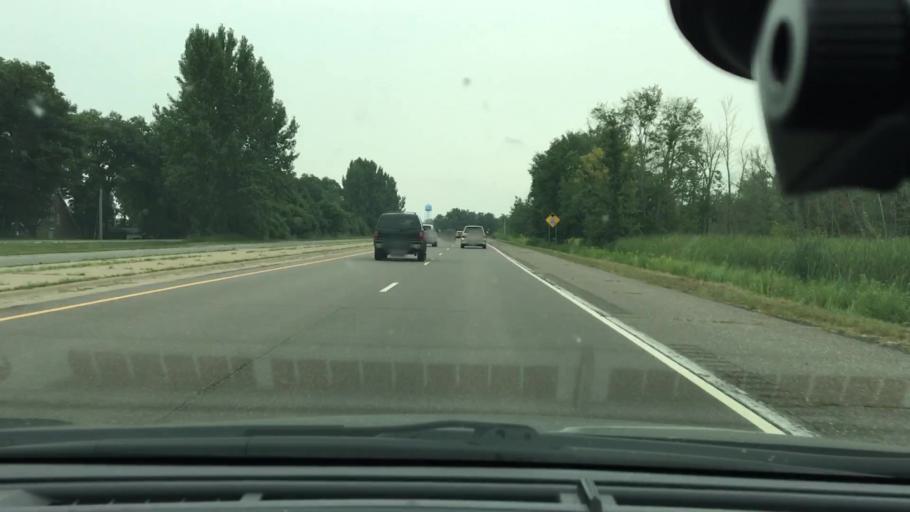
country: US
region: Minnesota
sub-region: Mille Lacs County
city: Vineland
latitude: 46.1947
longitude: -93.7629
